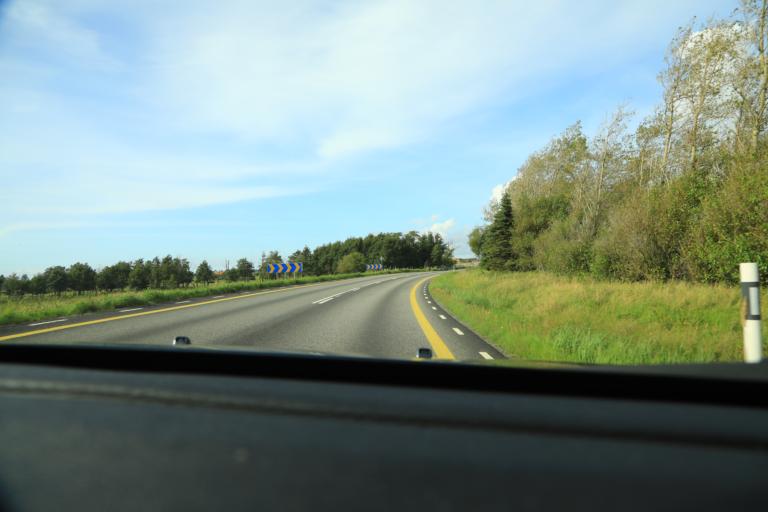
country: SE
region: Halland
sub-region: Varbergs Kommun
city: Traslovslage
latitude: 57.0253
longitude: 12.3351
